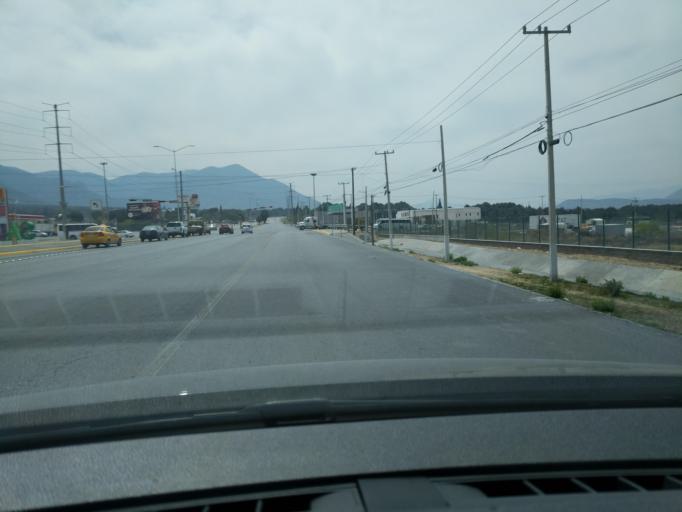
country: MX
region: Coahuila
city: Saltillo
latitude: 25.3540
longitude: -101.0220
